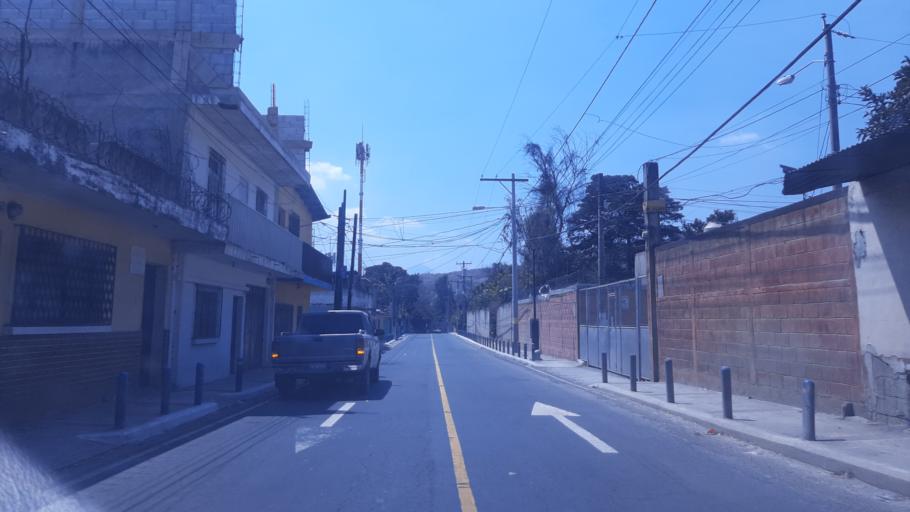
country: GT
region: Guatemala
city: Villa Nueva
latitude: 14.5227
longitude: -90.5929
